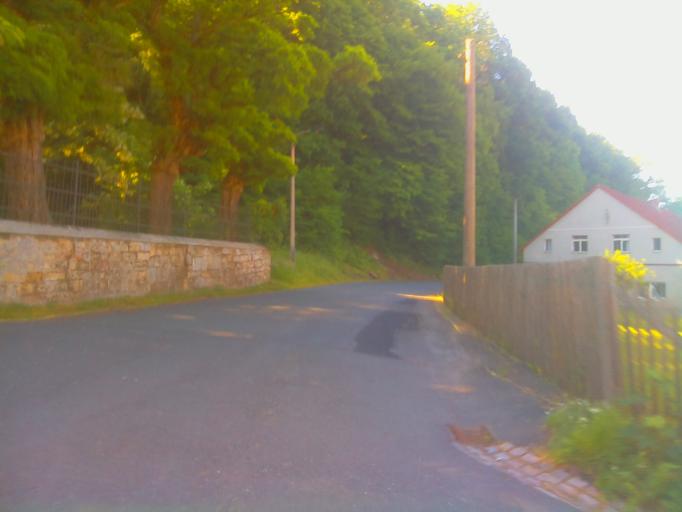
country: DE
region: Thuringia
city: Orlamunde
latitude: 50.7580
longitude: 11.5203
